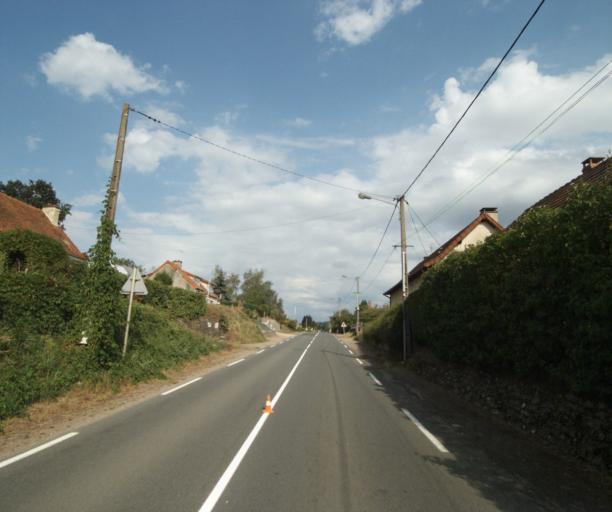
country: FR
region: Bourgogne
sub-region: Departement de Saone-et-Loire
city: Gueugnon
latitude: 46.6026
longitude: 4.0848
